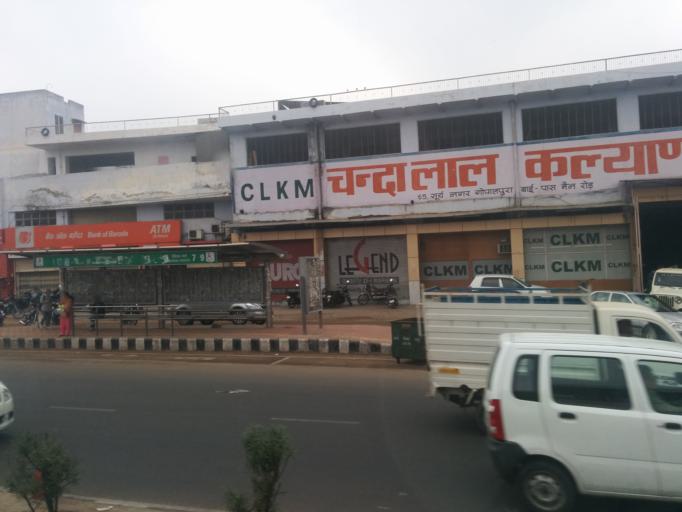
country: IN
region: Rajasthan
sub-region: Jaipur
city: Jaipur
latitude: 26.8747
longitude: 75.7756
